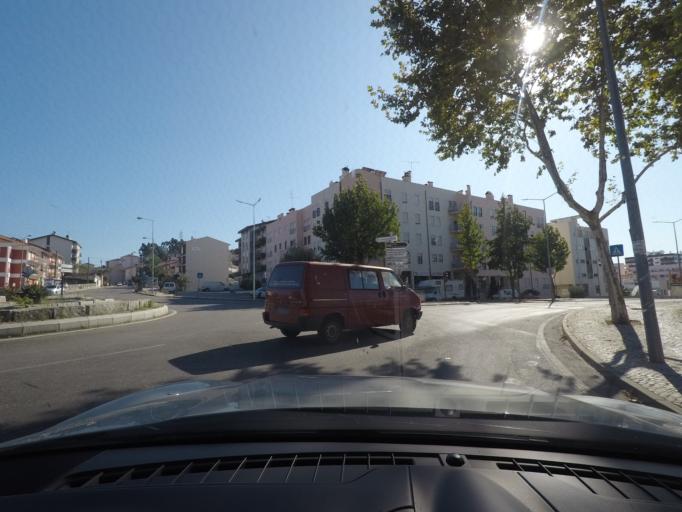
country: PT
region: Coimbra
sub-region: Coimbra
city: Coimbra
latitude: 40.1937
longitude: -8.4027
